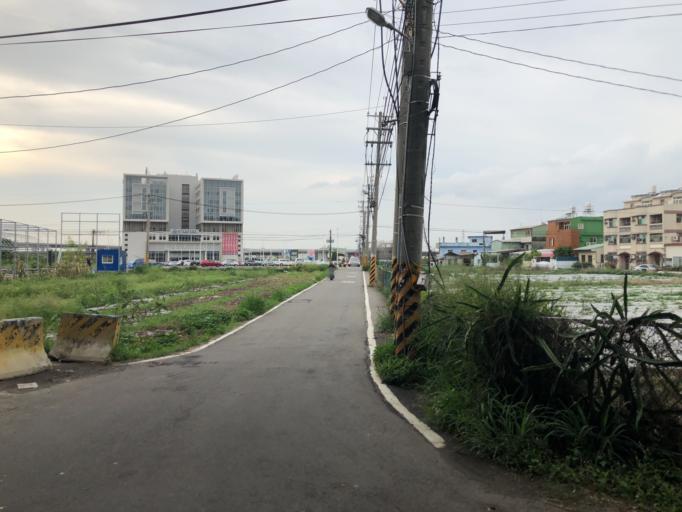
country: TW
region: Taiwan
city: Zhongxing New Village
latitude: 24.0515
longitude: 120.6885
